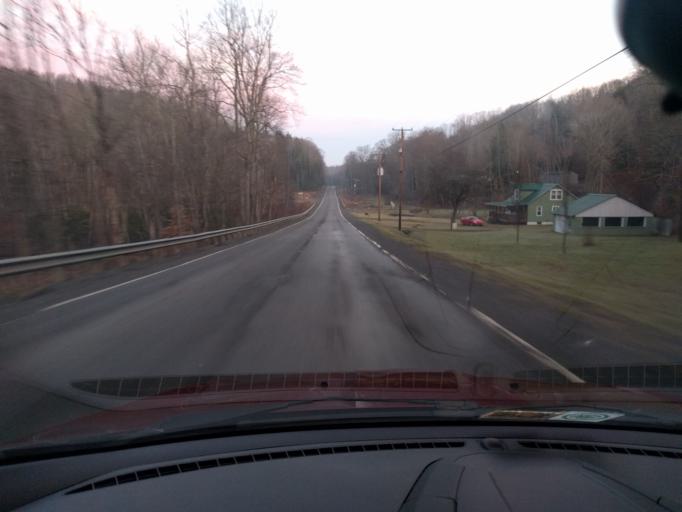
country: US
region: West Virginia
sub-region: Greenbrier County
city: Rainelle
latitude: 38.0297
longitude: -80.9156
